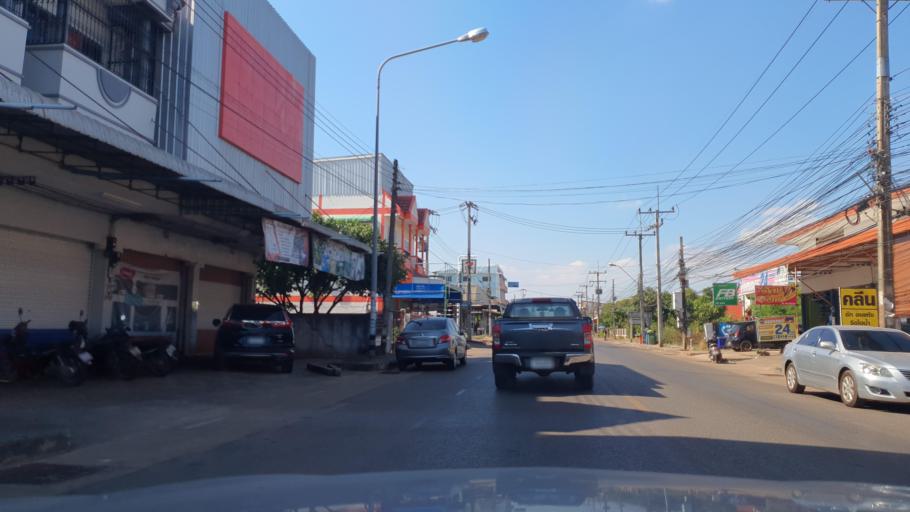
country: TH
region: Sakon Nakhon
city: Sakon Nakhon
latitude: 17.1622
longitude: 104.1265
